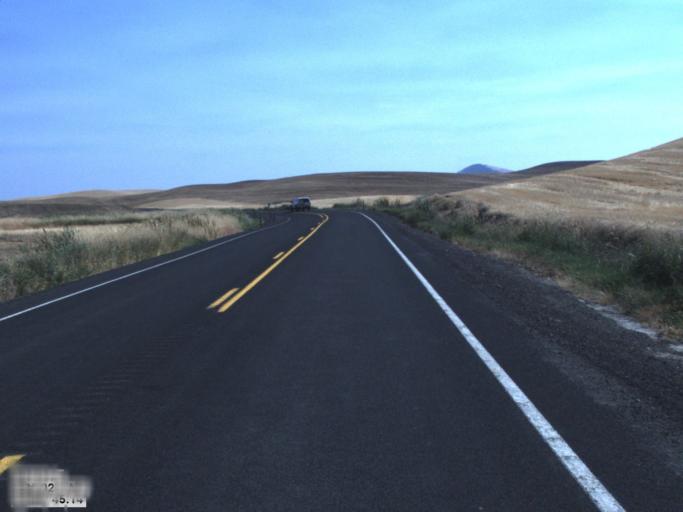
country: US
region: Idaho
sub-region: Benewah County
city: Plummer
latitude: 47.1935
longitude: -117.1131
